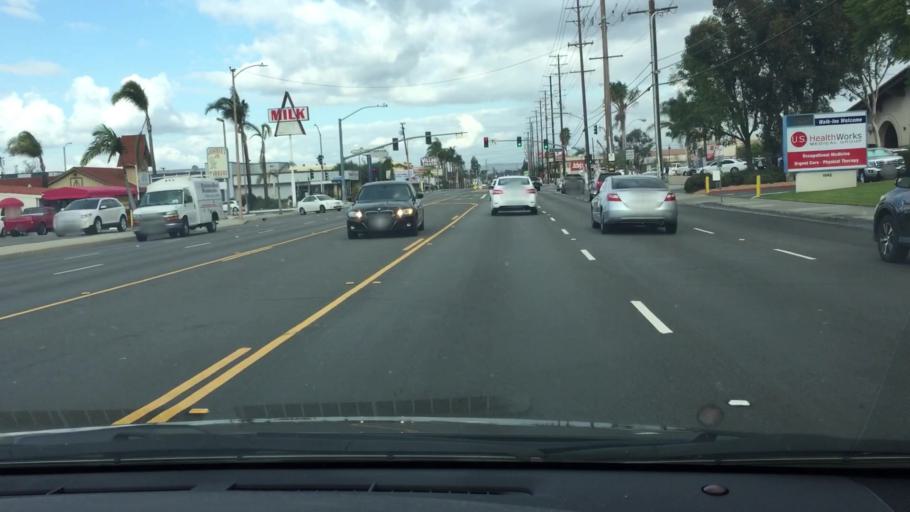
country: US
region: California
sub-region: Orange County
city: Orange
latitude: 33.8046
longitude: -117.8357
